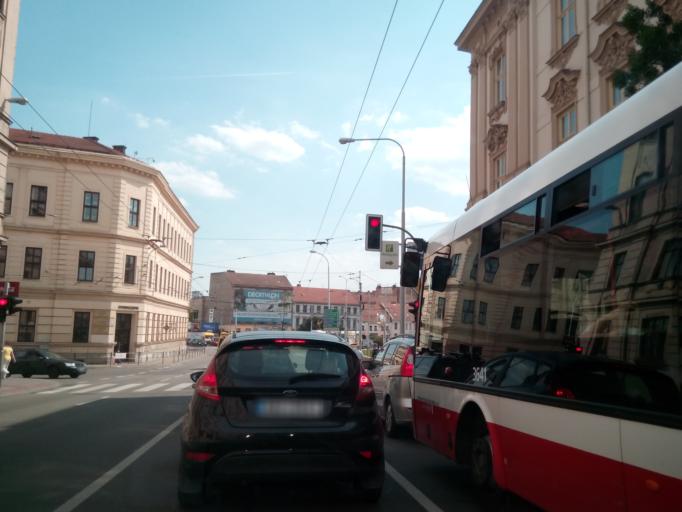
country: CZ
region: South Moravian
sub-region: Mesto Brno
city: Brno
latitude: 49.1919
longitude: 16.5956
